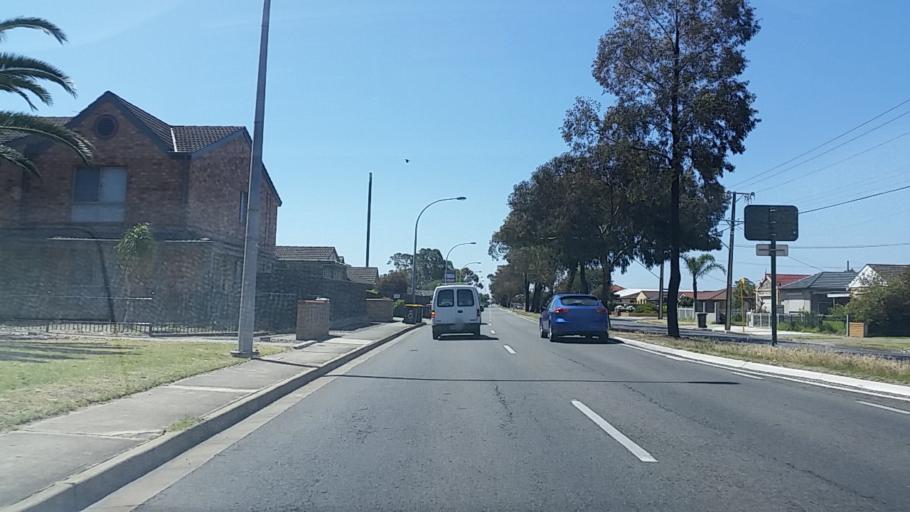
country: AU
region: South Australia
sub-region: Charles Sturt
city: Royal Park
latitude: -34.8781
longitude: 138.5035
